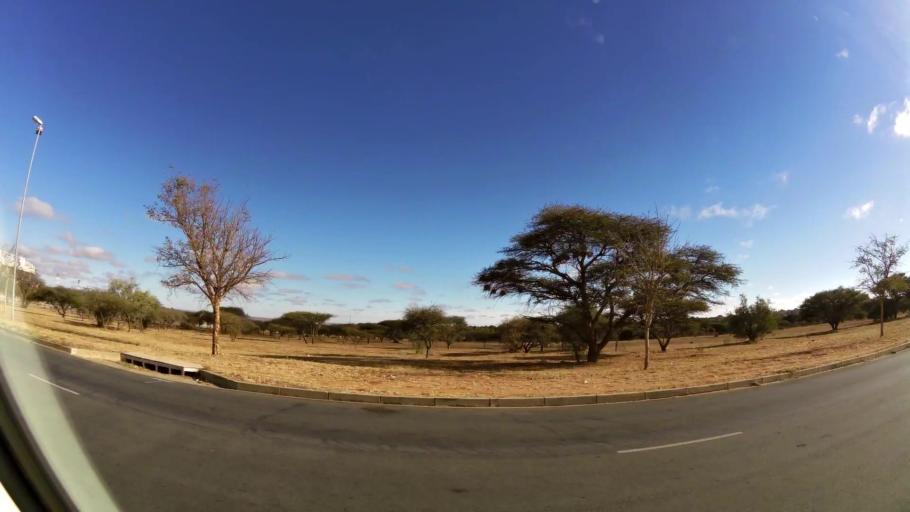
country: ZA
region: Limpopo
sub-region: Capricorn District Municipality
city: Polokwane
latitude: -23.9229
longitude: 29.4734
